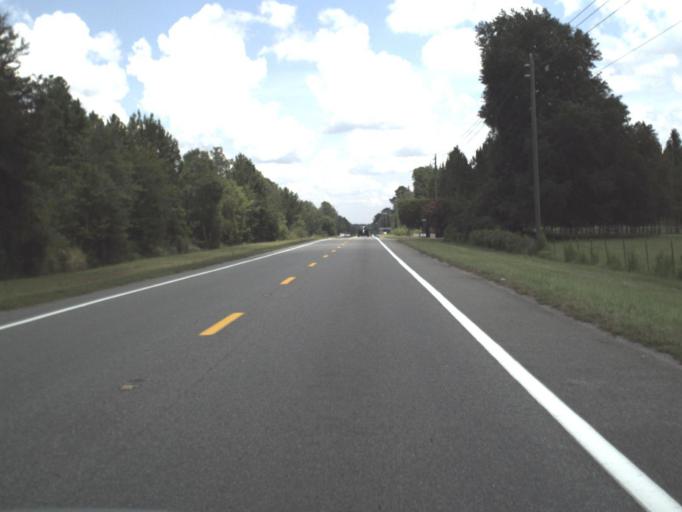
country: US
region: Florida
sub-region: Union County
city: Lake Butler
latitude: 30.0537
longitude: -82.2573
